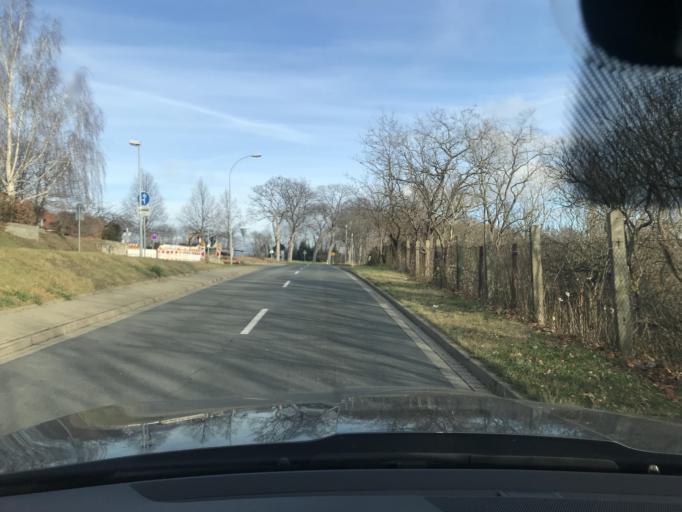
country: DE
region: Saxony-Anhalt
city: Weddersleben
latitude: 51.7650
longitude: 11.0884
